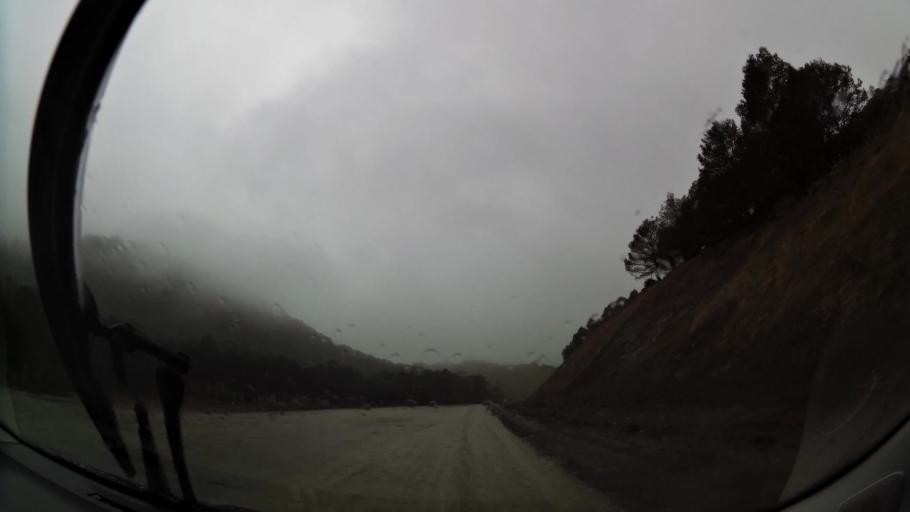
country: MA
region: Taza-Al Hoceima-Taounate
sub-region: Taza
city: Aknoul
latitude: 34.7568
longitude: -3.8033
